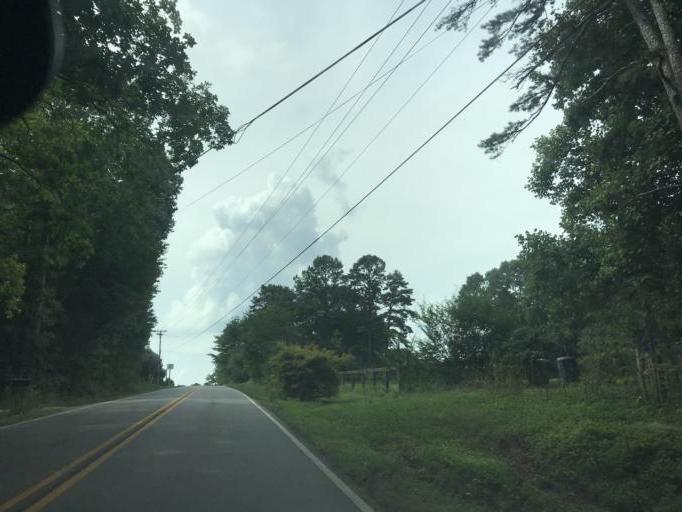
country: US
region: Georgia
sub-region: Forsyth County
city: Cumming
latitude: 34.2172
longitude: -84.2382
